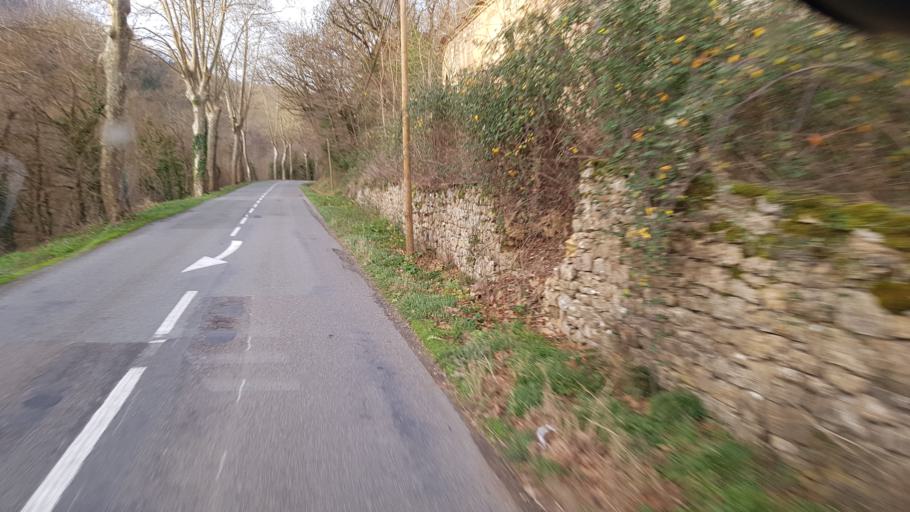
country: FR
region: Midi-Pyrenees
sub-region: Departement du Tarn-et-Garonne
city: Montricoux
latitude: 44.0017
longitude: 1.6865
